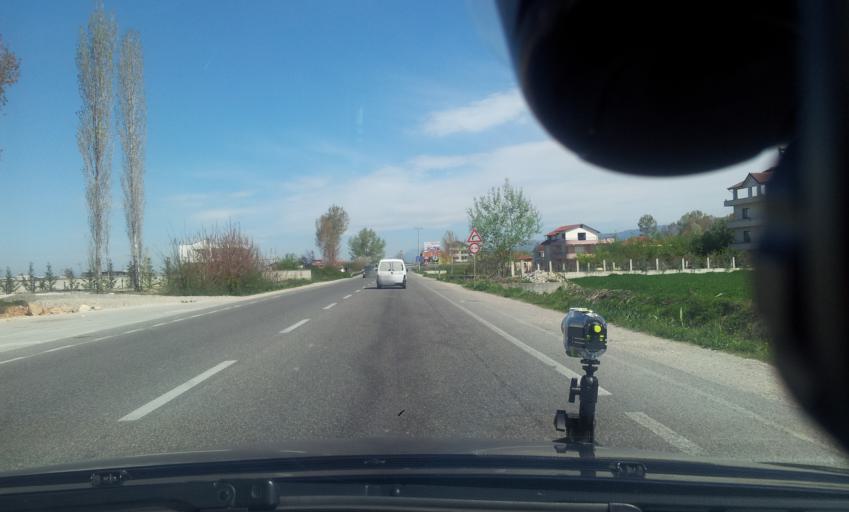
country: AL
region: Durres
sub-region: Rrethi i Krujes
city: Hasan
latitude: 41.4619
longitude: 19.6895
